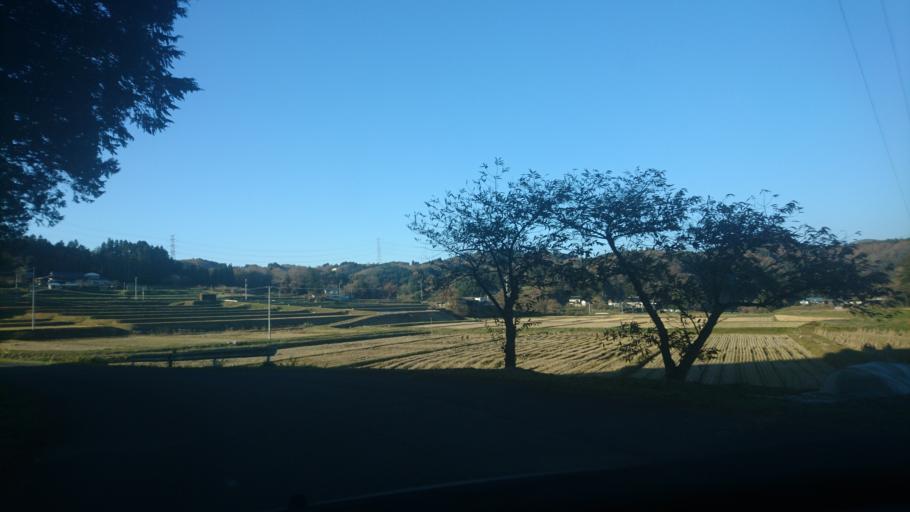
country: JP
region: Iwate
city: Ichinoseki
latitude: 38.9060
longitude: 141.2267
